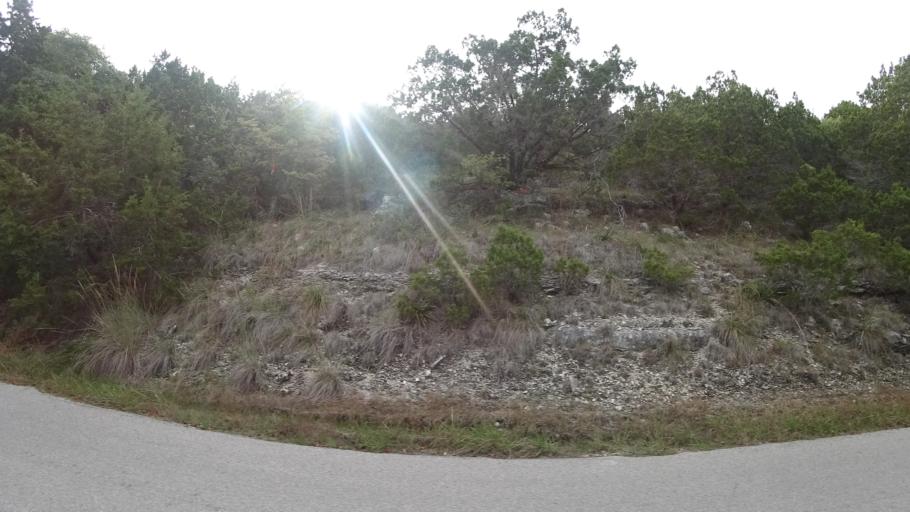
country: US
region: Texas
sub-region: Travis County
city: Hudson Bend
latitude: 30.3936
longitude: -97.8797
